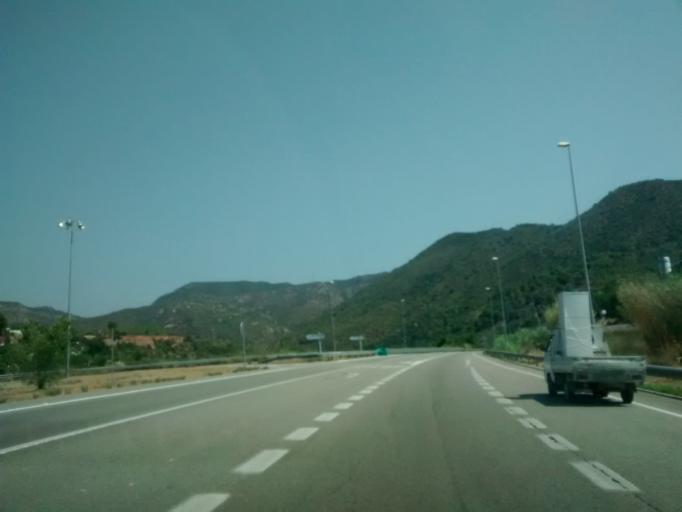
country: ES
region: Catalonia
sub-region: Provincia de Barcelona
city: Olesa de Montserrat
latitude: 41.5552
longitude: 1.8789
